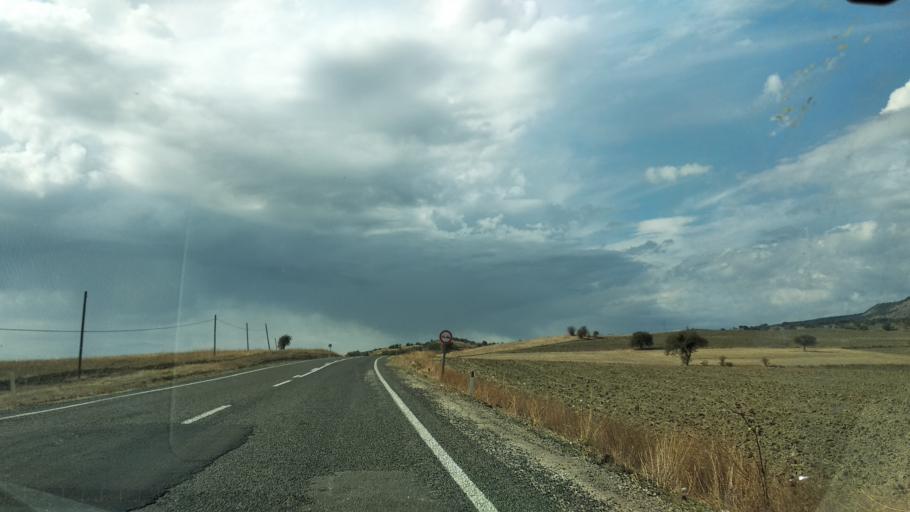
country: TR
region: Bolu
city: Seben
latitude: 40.3891
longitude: 31.5428
